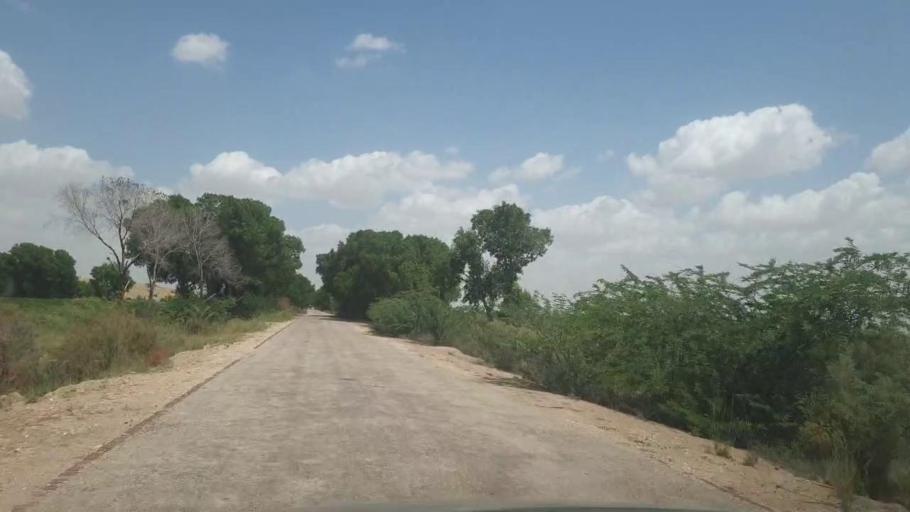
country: PK
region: Sindh
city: Kot Diji
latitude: 27.2202
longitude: 69.0441
